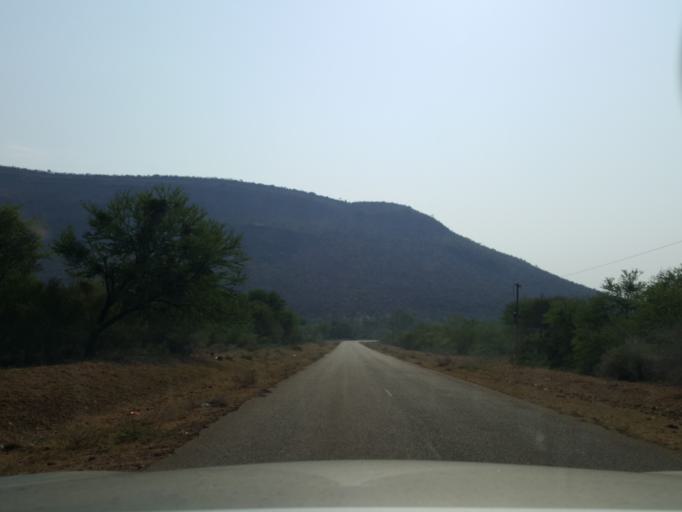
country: BW
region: South East
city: Lobatse
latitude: -25.3279
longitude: 25.7692
